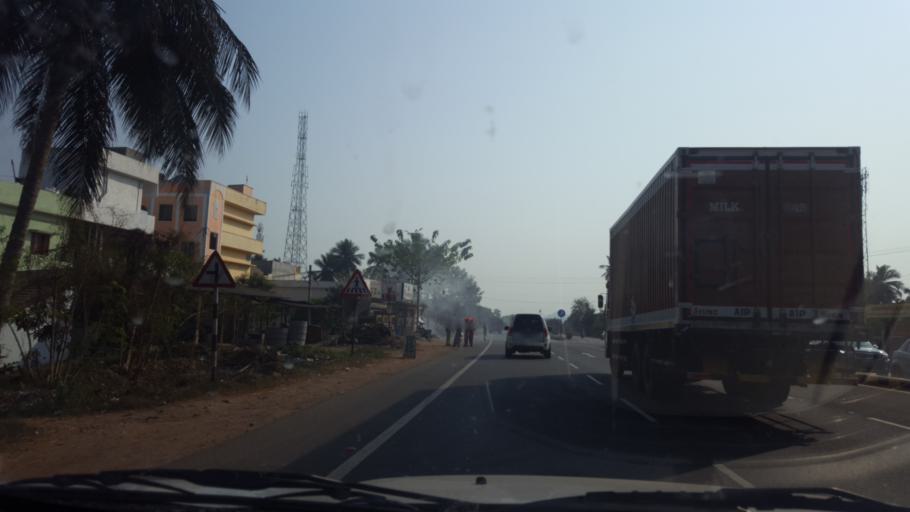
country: IN
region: Andhra Pradesh
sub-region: Vishakhapatnam
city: Elamanchili
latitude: 17.5959
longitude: 82.8725
